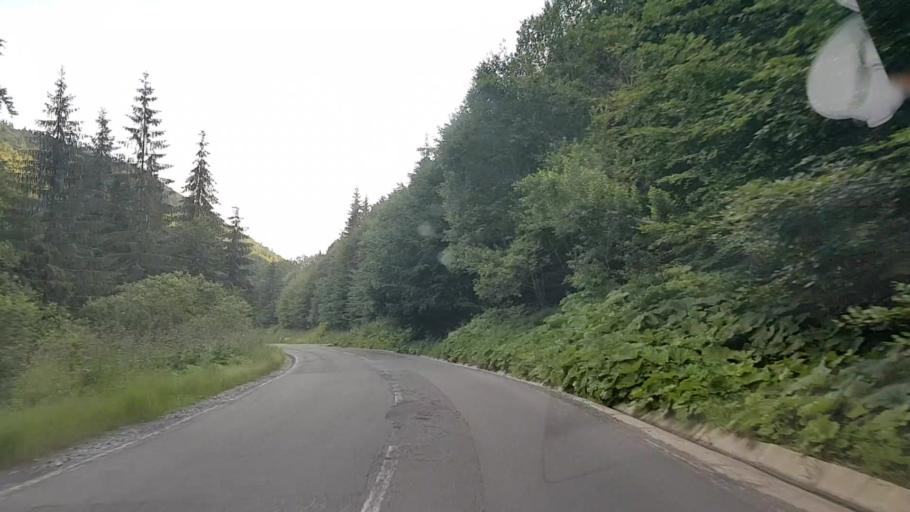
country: RO
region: Harghita
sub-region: Comuna Praid
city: Ocna de Sus
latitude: 46.6222
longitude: 25.2515
